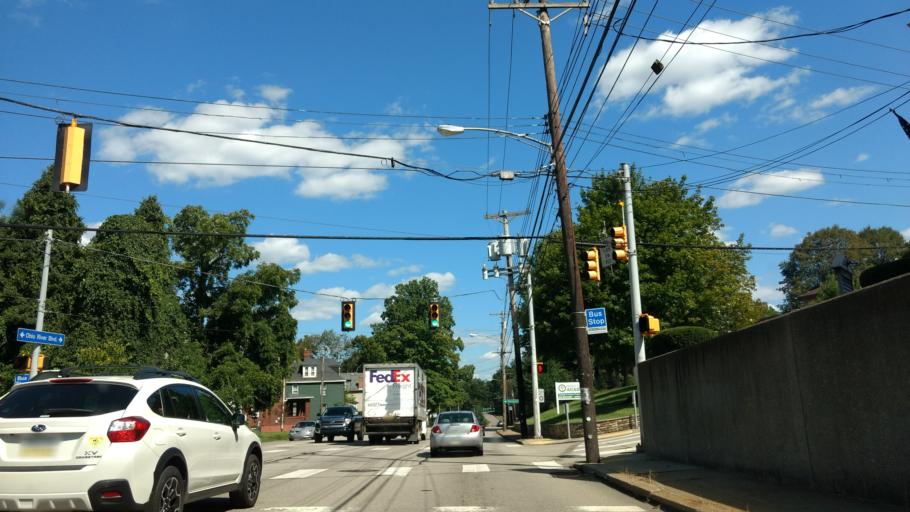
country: US
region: Pennsylvania
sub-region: Allegheny County
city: Emsworth
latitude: 40.5115
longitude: -80.1012
